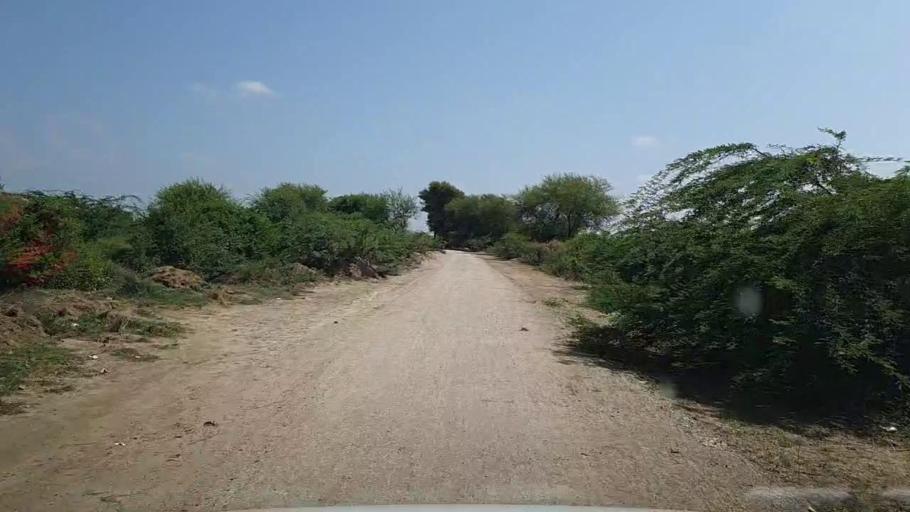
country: PK
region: Sindh
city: Kario
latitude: 24.8436
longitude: 68.6996
